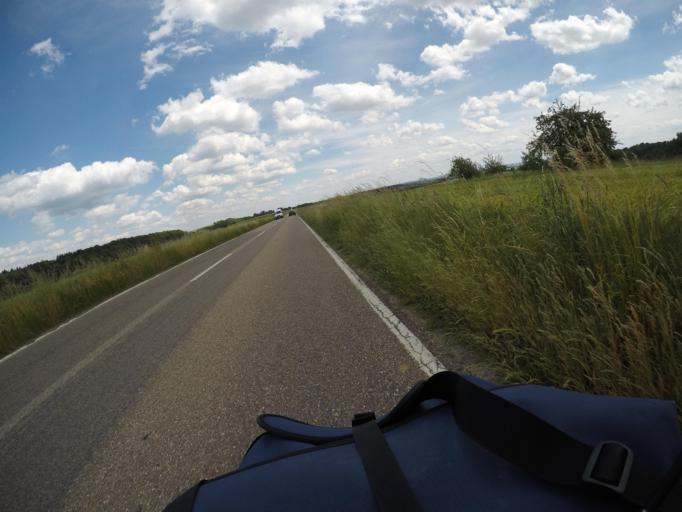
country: DE
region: Baden-Wuerttemberg
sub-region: Regierungsbezirk Stuttgart
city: Kirchardt
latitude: 49.2311
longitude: 9.0322
